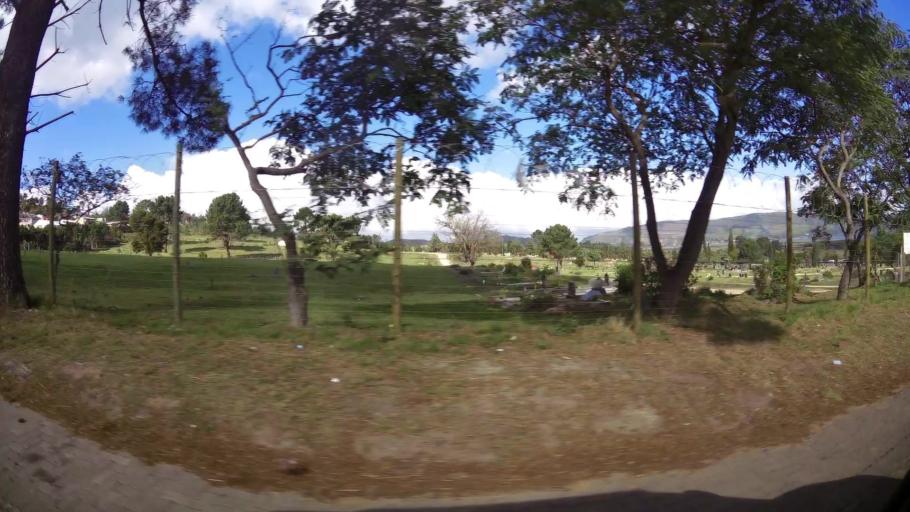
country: ZA
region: Western Cape
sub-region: Eden District Municipality
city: Knysna
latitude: -34.0479
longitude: 23.0798
